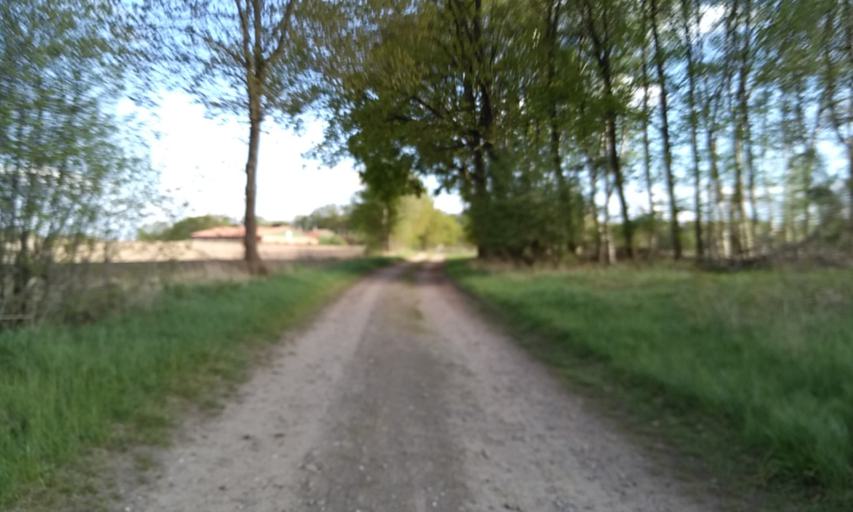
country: DE
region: Lower Saxony
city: Regesbostel
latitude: 53.4082
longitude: 9.6547
